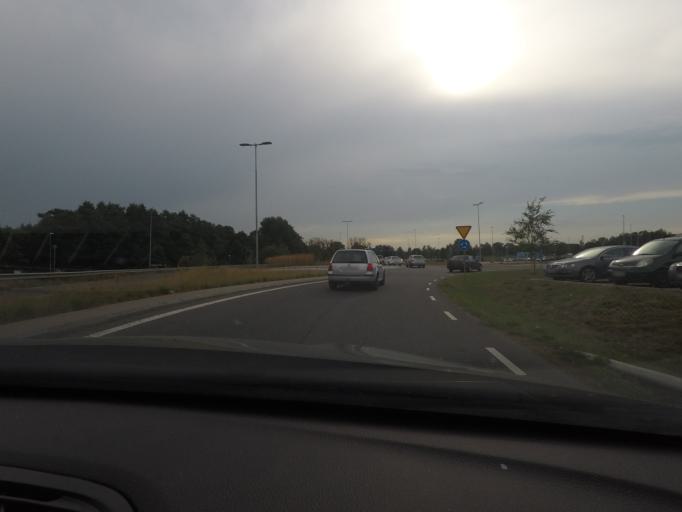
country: SE
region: Halland
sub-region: Halmstads Kommun
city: Fyllinge
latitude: 56.6540
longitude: 12.9119
